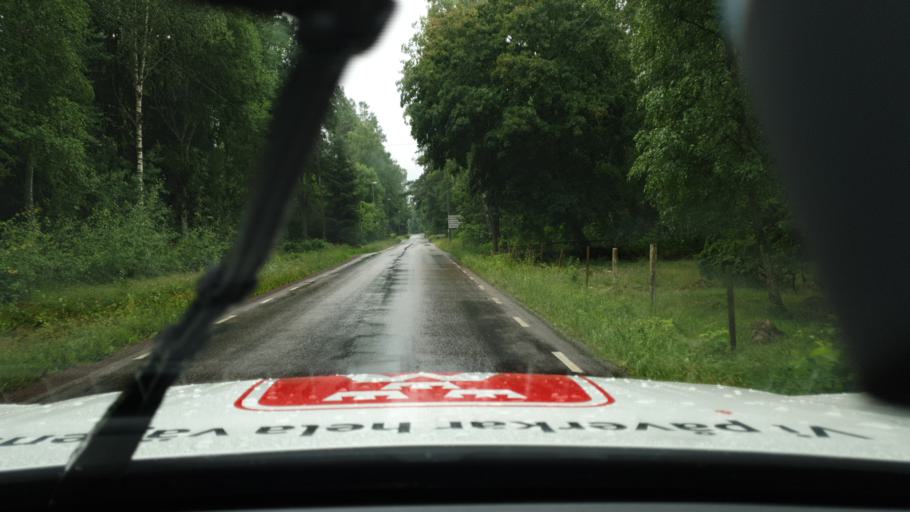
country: SE
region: Vaestra Goetaland
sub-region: Falkopings Kommun
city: Floby
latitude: 58.1518
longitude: 13.3314
